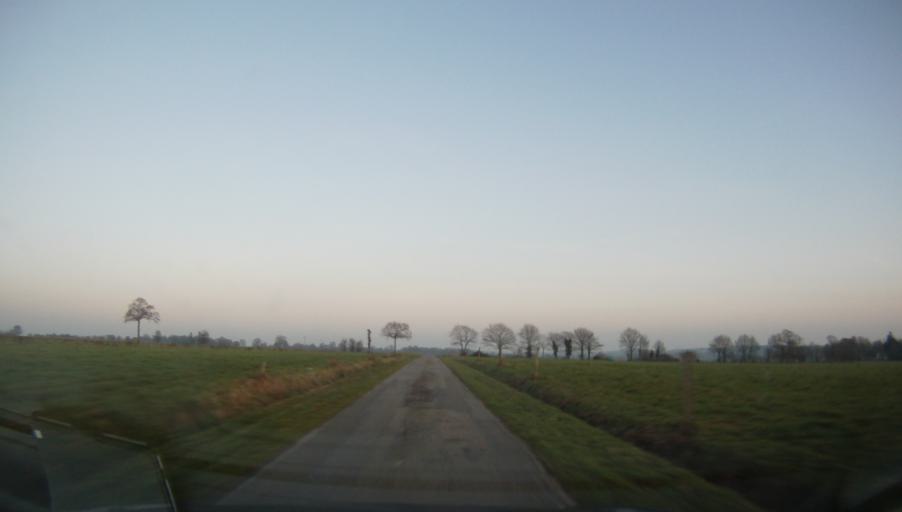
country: FR
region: Brittany
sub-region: Departement d'Ille-et-Vilaine
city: Crevin
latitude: 47.9312
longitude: -1.6471
